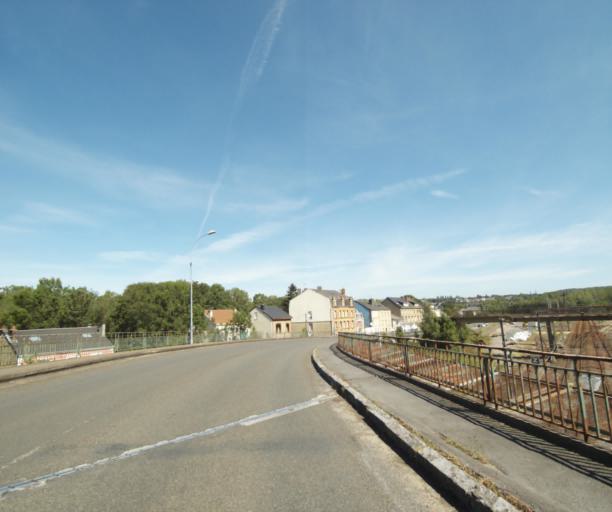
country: FR
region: Champagne-Ardenne
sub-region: Departement des Ardennes
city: Villers-Semeuse
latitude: 49.7443
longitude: 4.7350
